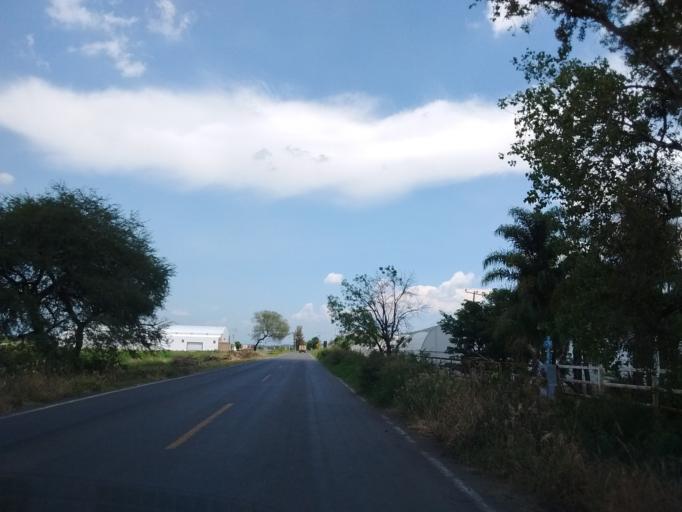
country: MX
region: Jalisco
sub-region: Atotonilco el Alto
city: Vistas del Maguey [Fraccionamiento]
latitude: 20.4997
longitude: -102.5292
